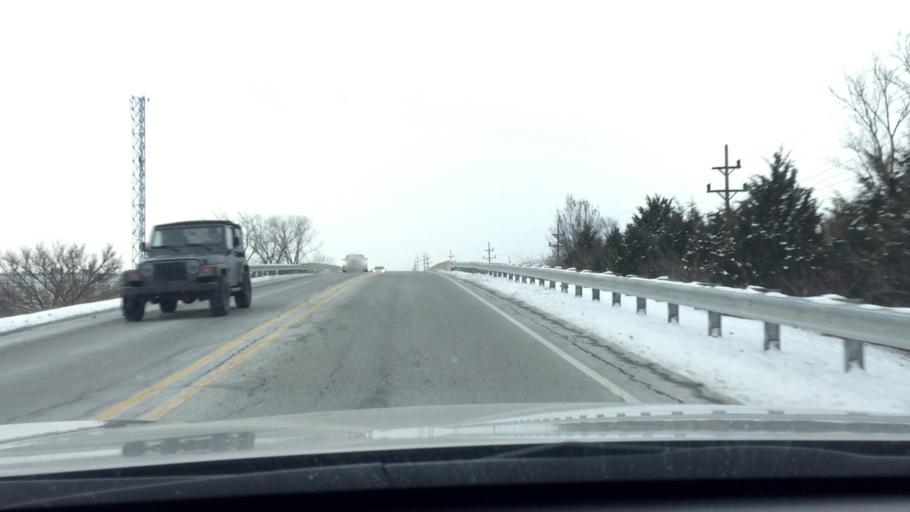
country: US
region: Indiana
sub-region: Hamilton County
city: Fishers
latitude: 39.9682
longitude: -85.9942
